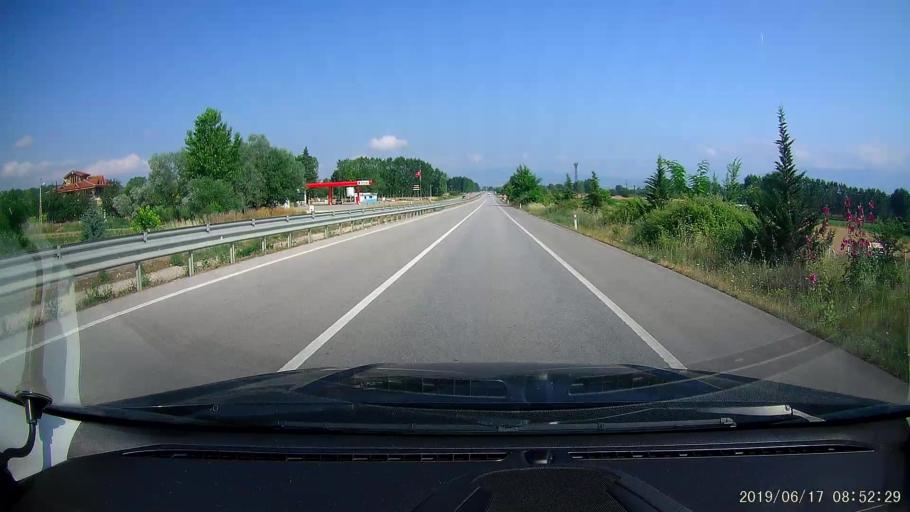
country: TR
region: Tokat
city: Erbaa
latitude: 40.6983
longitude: 36.4959
